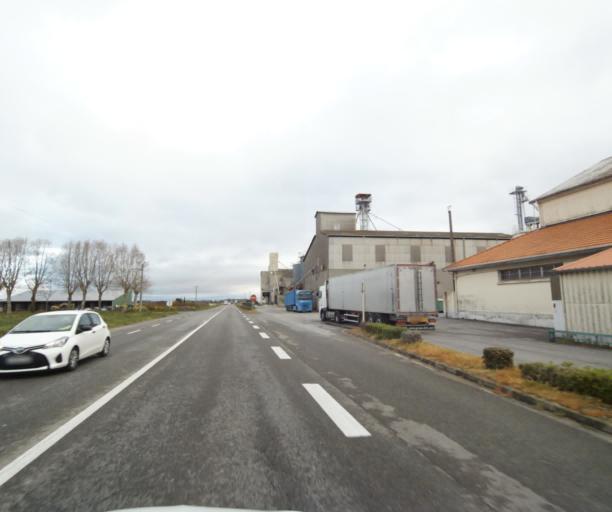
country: FR
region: Midi-Pyrenees
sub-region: Departement de l'Ariege
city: Saverdun
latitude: 43.1973
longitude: 1.6099
